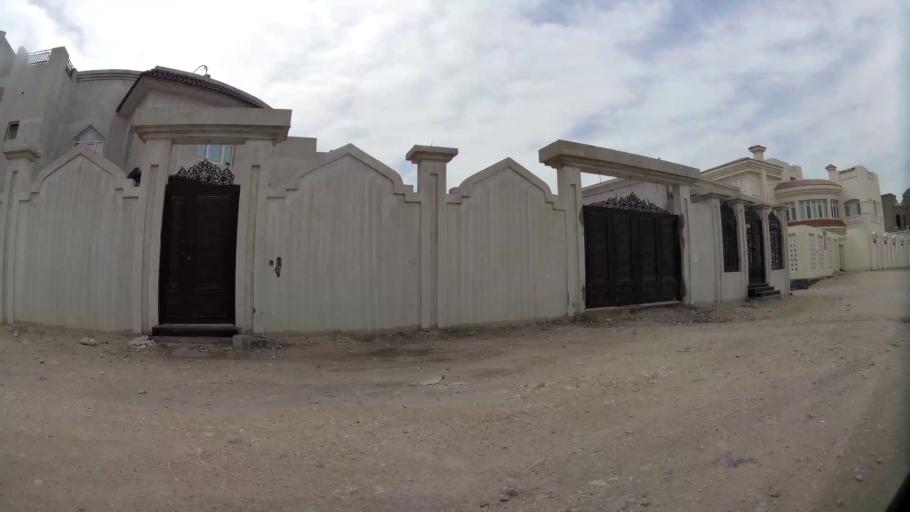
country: QA
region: Baladiyat ad Dawhah
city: Doha
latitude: 25.2136
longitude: 51.4939
